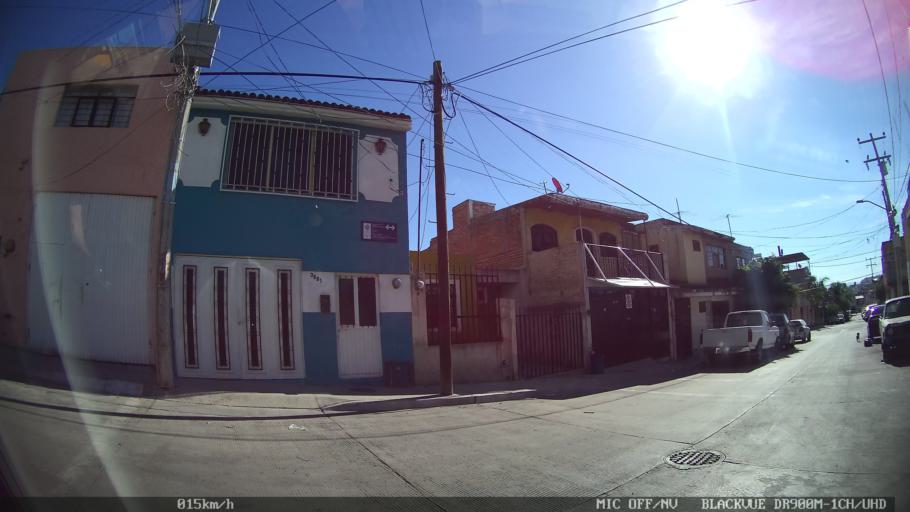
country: MX
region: Jalisco
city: Tlaquepaque
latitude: 20.6932
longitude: -103.2759
